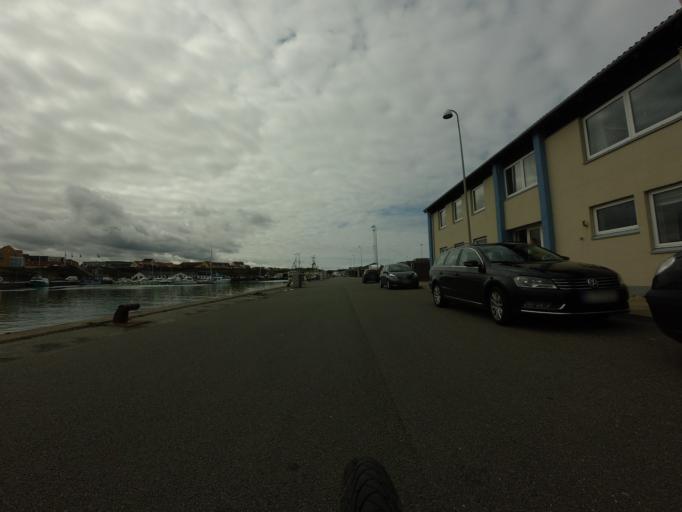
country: DK
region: North Denmark
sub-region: Hjorring Kommune
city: Hirtshals
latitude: 57.5936
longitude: 9.9568
